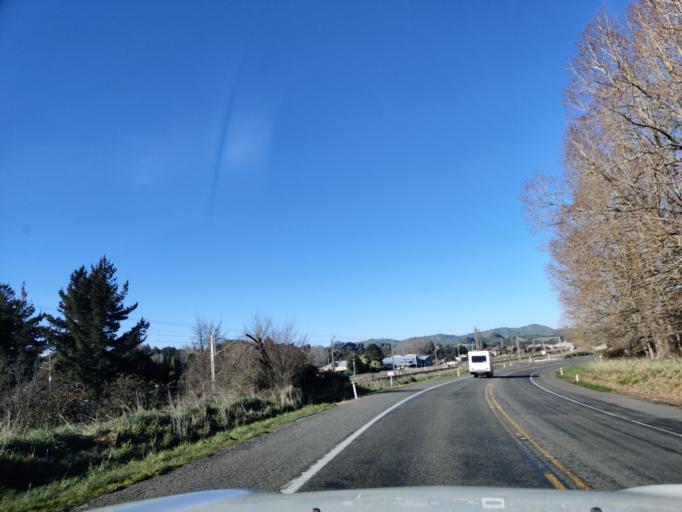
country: NZ
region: Manawatu-Wanganui
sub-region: Ruapehu District
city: Waiouru
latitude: -39.7318
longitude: 175.8441
